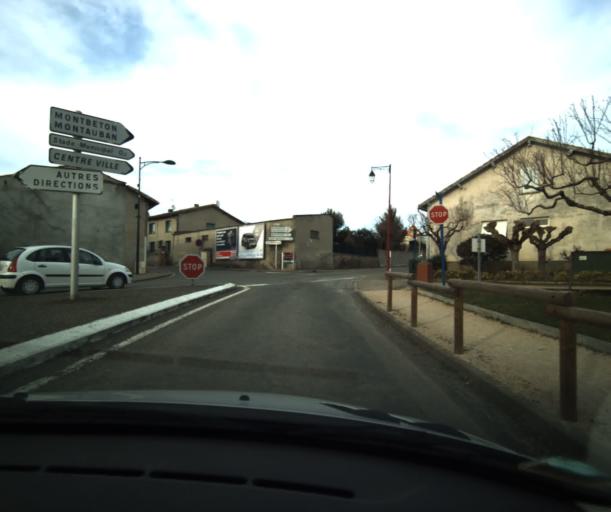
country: FR
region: Midi-Pyrenees
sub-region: Departement du Tarn-et-Garonne
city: Montech
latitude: 43.9542
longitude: 1.2313
